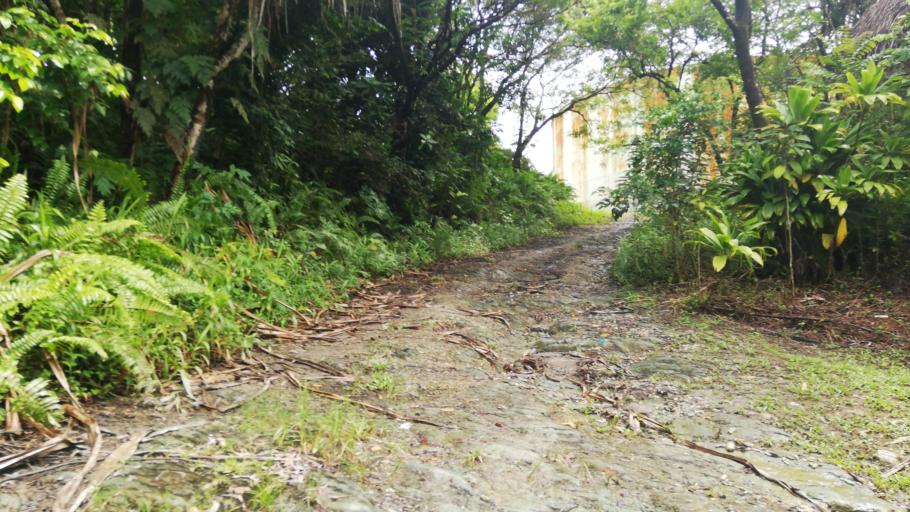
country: FM
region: Yap
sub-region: Weloy Municipality
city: Colonia
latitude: 9.5171
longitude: 138.0986
